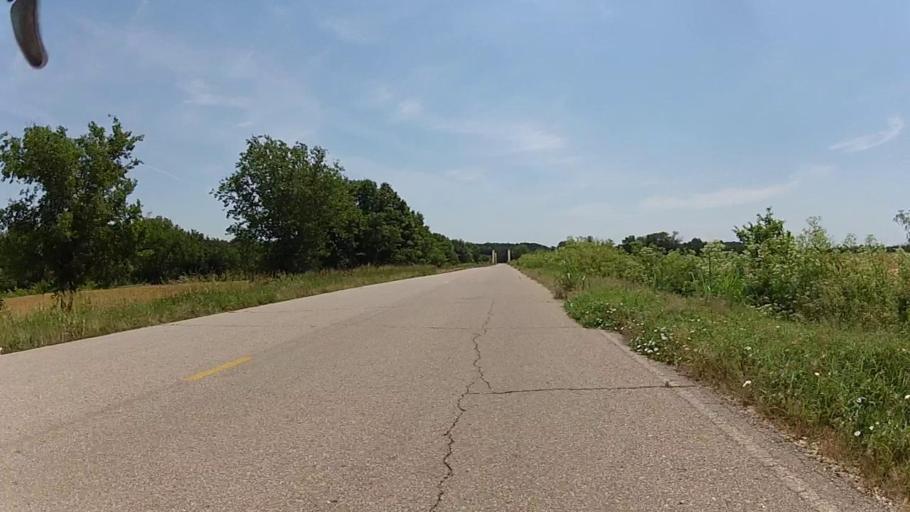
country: US
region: Kansas
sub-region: Chautauqua County
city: Sedan
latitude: 37.1063
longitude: -96.4868
